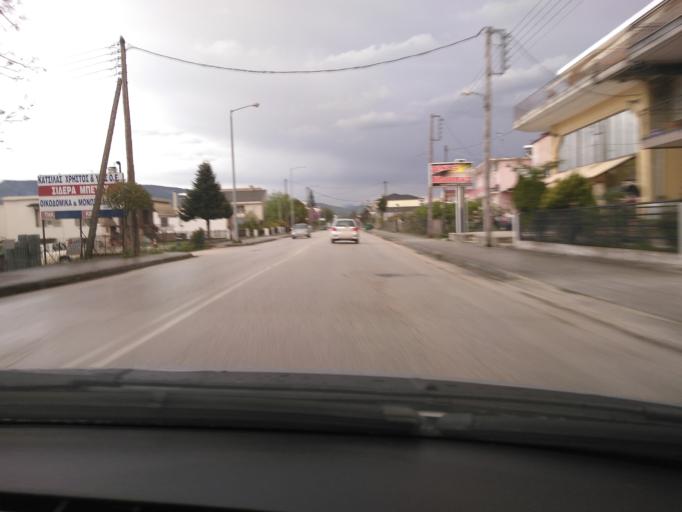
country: GR
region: Epirus
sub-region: Nomos Ioanninon
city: Katsikas
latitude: 39.6284
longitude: 20.8810
